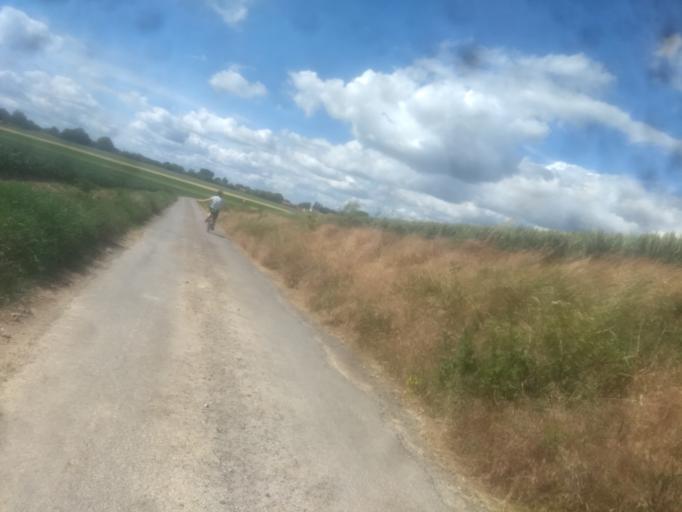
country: FR
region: Nord-Pas-de-Calais
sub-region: Departement du Pas-de-Calais
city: Tilloy-les-Mofflaines
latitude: 50.2424
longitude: 2.8303
